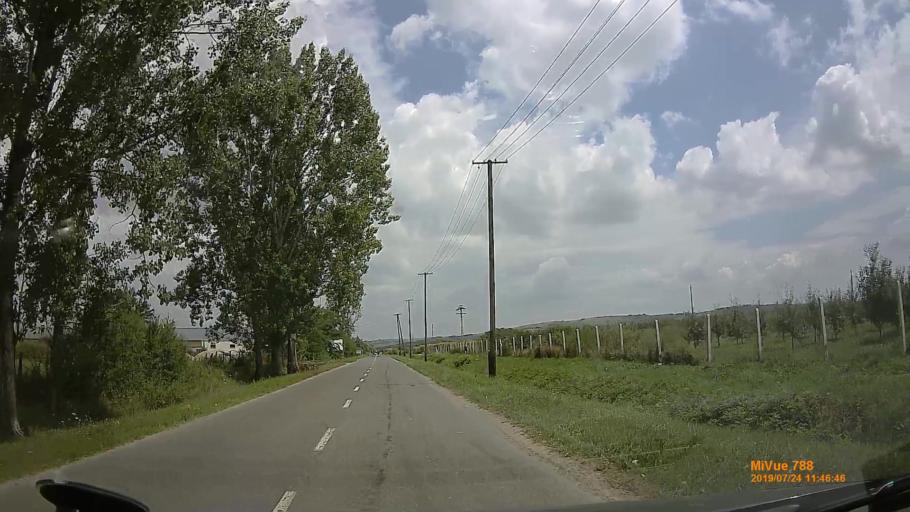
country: UA
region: Zakarpattia
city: Batiovo
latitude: 48.2401
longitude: 22.4369
